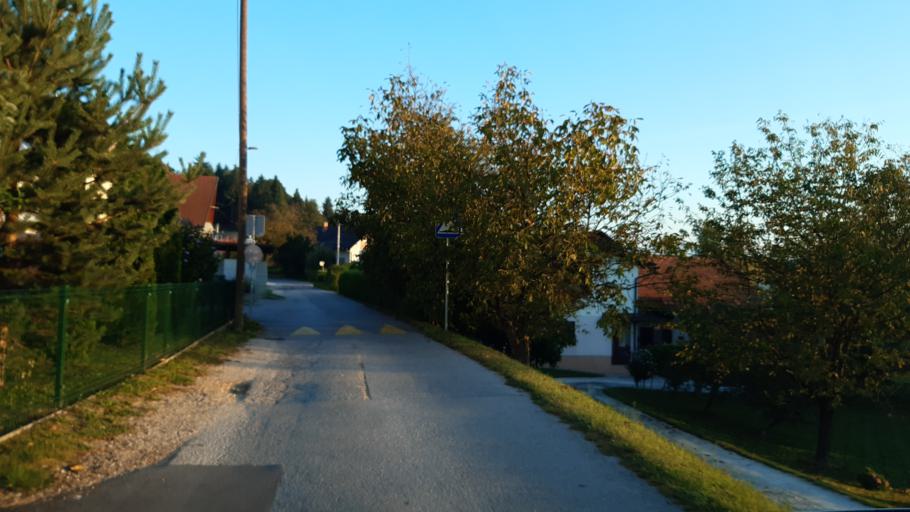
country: SI
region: Medvode
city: Zgornje Pirnice
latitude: 46.1095
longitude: 14.4362
